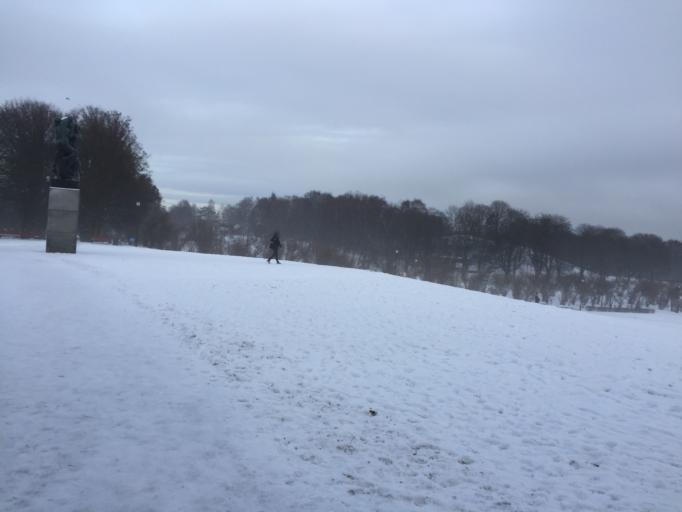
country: NO
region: Oslo
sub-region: Oslo
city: Sjolyststranda
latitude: 59.9283
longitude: 10.6960
